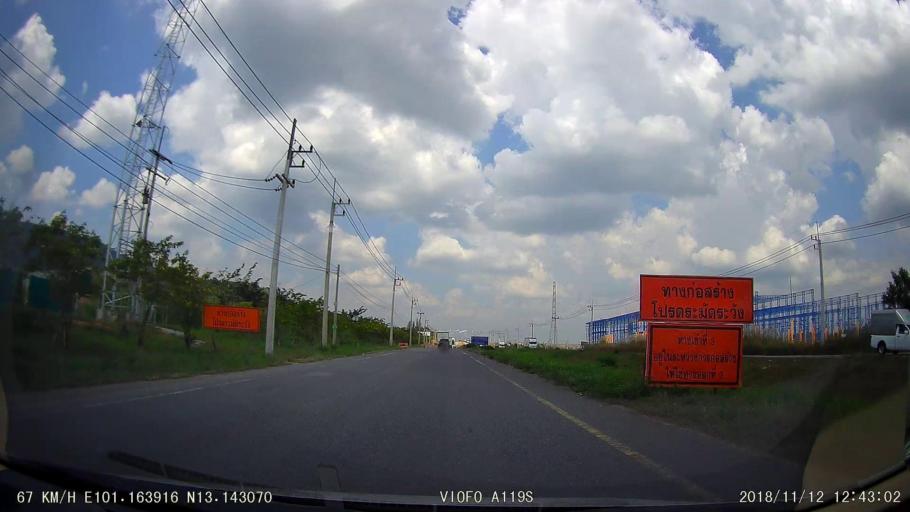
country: TH
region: Chon Buri
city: Ban Bueng
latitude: 13.1560
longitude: 101.1630
